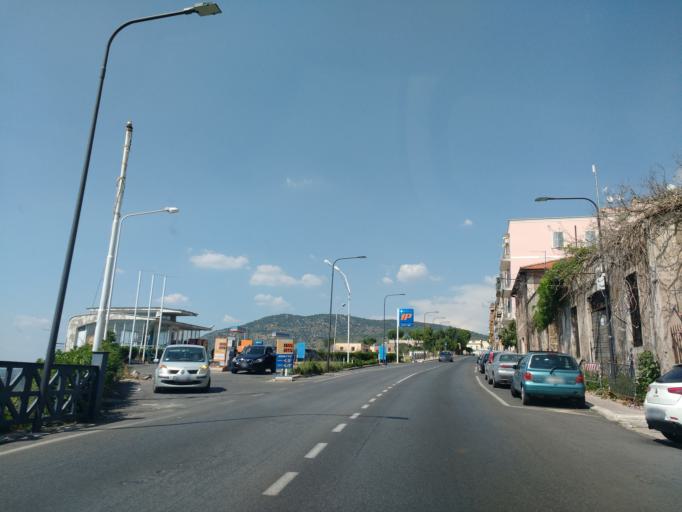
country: IT
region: Latium
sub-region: Citta metropolitana di Roma Capitale
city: Tivoli
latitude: 41.9561
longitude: 12.7923
